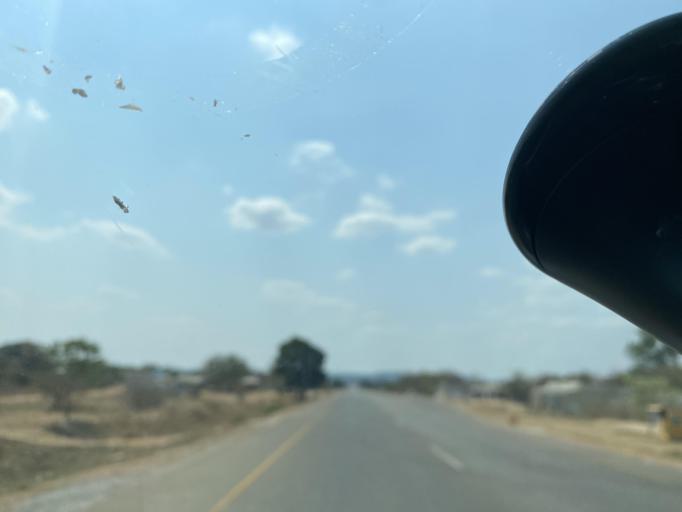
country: ZM
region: Lusaka
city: Chongwe
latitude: -15.5664
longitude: 28.6915
